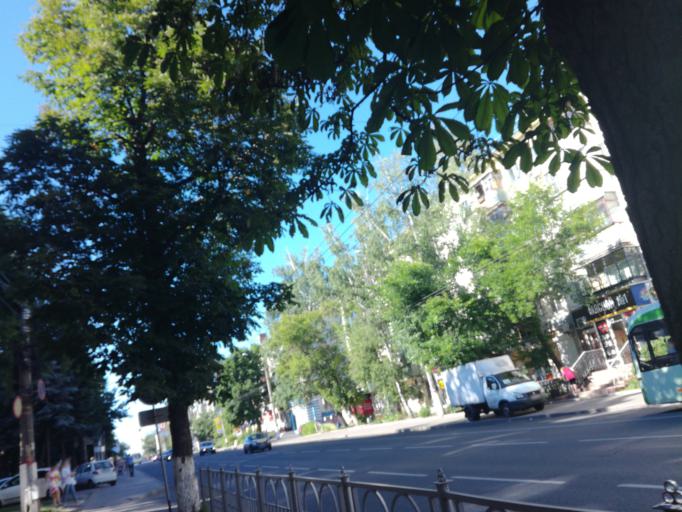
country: RU
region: Kursk
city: Kursk
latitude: 51.7423
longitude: 36.1903
